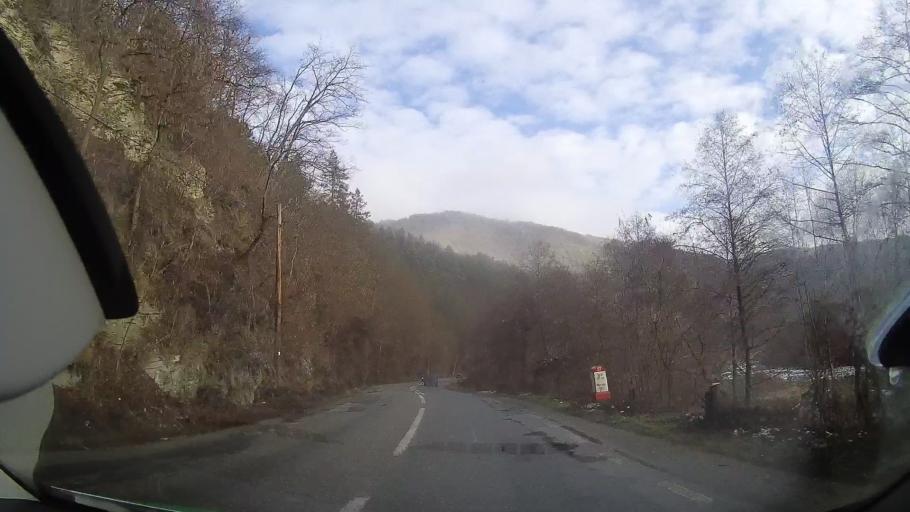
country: RO
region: Alba
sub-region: Comuna Lupsa
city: Lupsa
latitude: 46.3848
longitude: 23.2317
